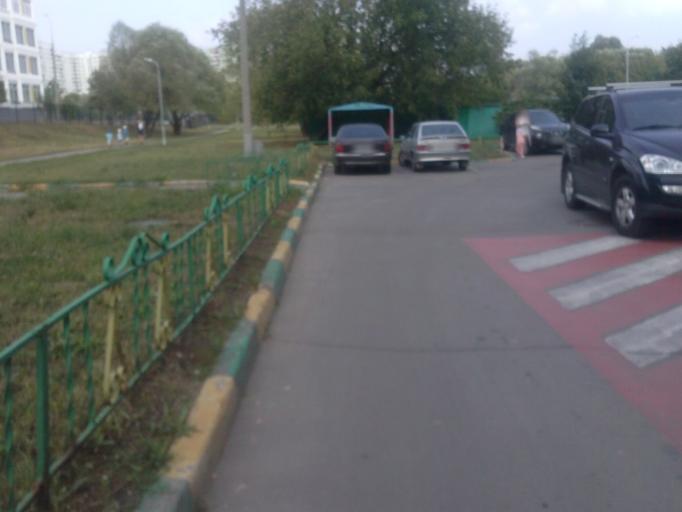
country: RU
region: Moskovskaya
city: Bol'shaya Setun'
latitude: 55.7155
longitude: 37.4155
